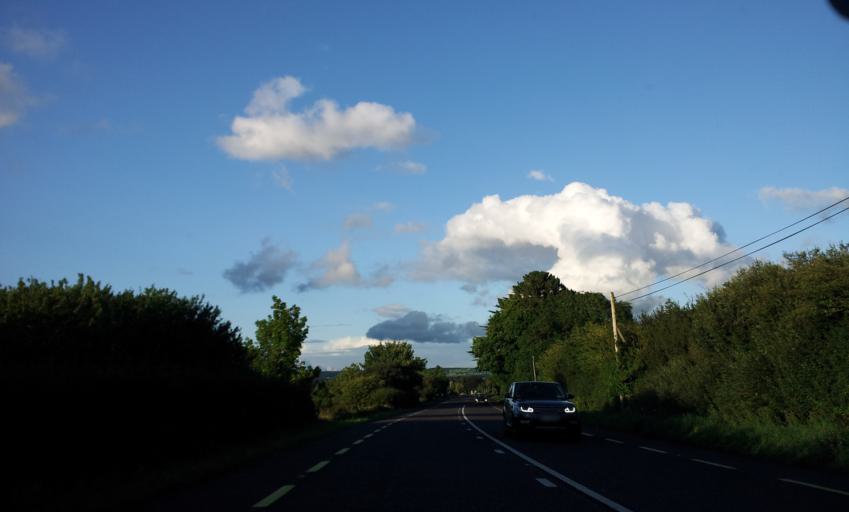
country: IE
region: Munster
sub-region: County Limerick
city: Abbeyfeale
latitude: 52.3682
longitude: -9.3206
